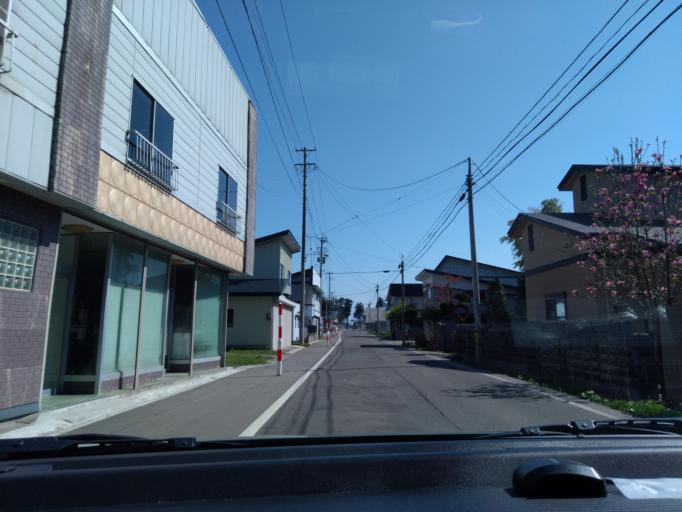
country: JP
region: Akita
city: Kakunodatemachi
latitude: 39.5557
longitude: 140.5859
